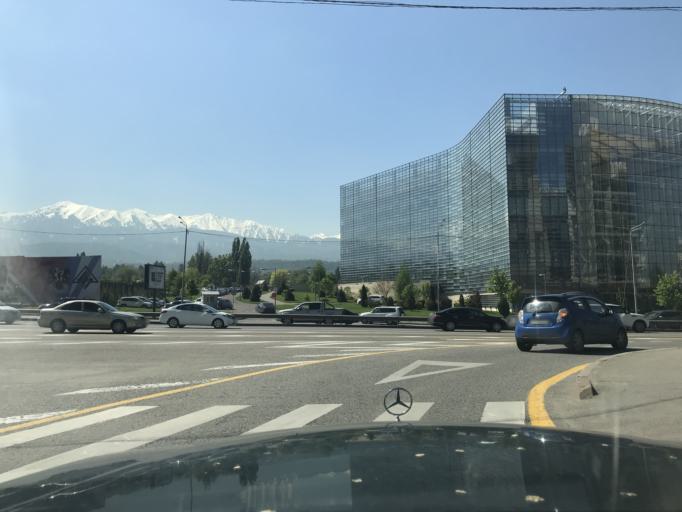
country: KZ
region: Almaty Qalasy
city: Almaty
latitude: 43.2283
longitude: 76.9443
